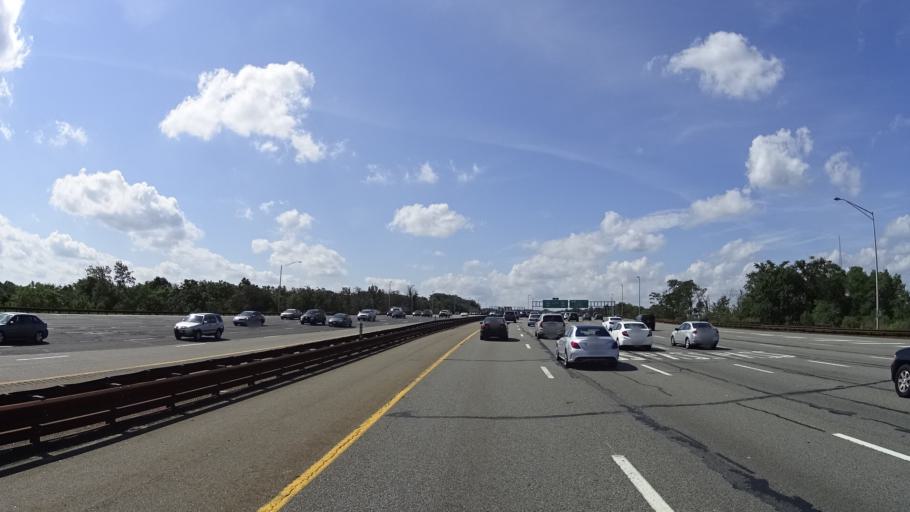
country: US
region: New Jersey
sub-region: Middlesex County
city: South Amboy
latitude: 40.4930
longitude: -74.3008
